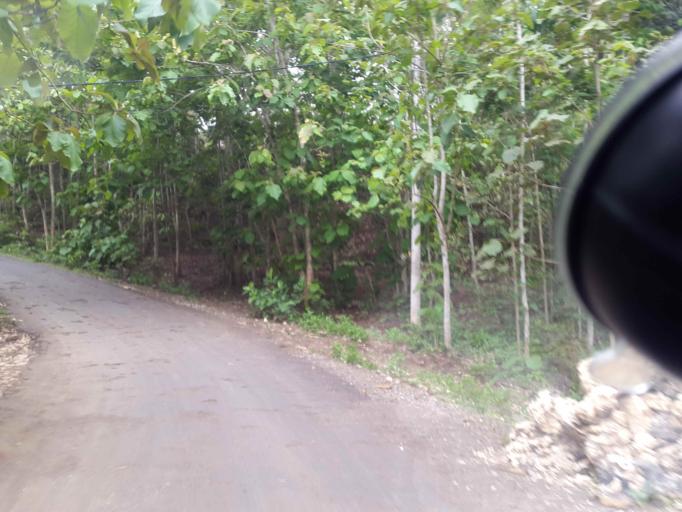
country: ID
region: East Java
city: Miribanteng
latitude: -8.2358
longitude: 112.0201
